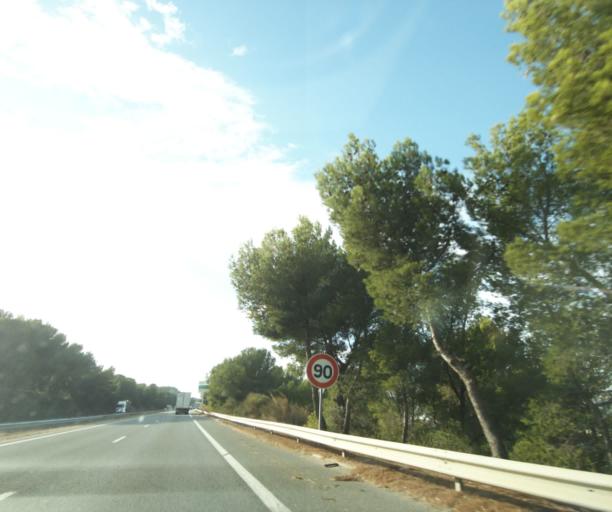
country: FR
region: Provence-Alpes-Cote d'Azur
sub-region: Departement des Bouches-du-Rhone
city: Martigues
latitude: 43.3990
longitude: 5.0889
